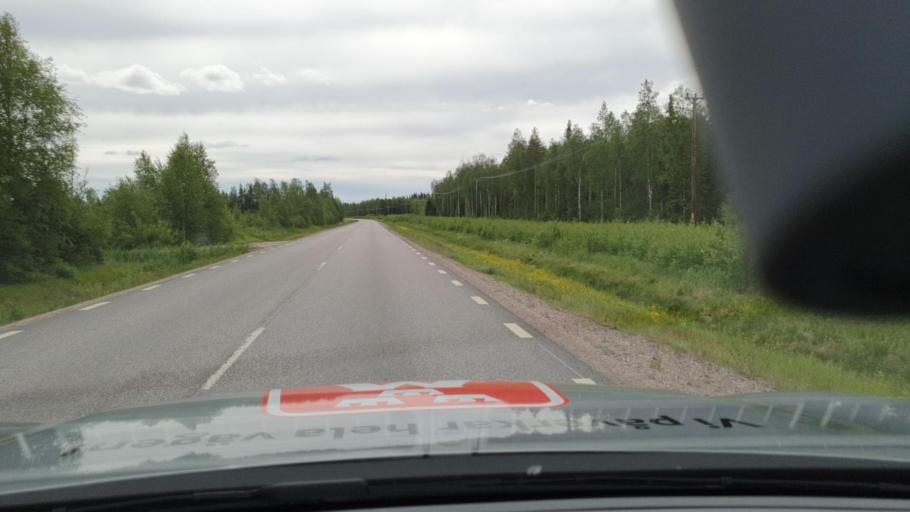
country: SE
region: Norrbotten
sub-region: Kalix Kommun
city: Kalix
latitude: 65.9010
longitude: 23.4599
